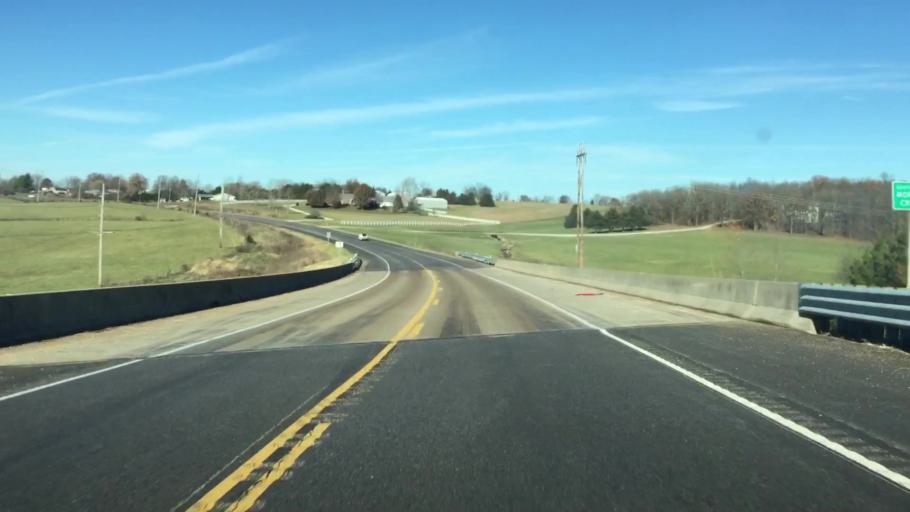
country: US
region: Missouri
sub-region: Miller County
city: Eldon
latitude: 38.3706
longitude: -92.6173
